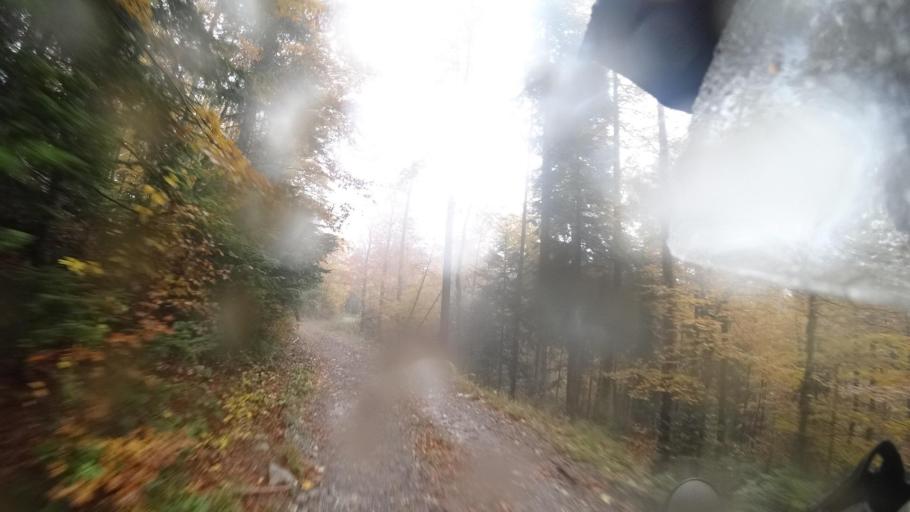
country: HR
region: Primorsko-Goranska
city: Vrbovsko
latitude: 45.2914
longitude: 15.0494
